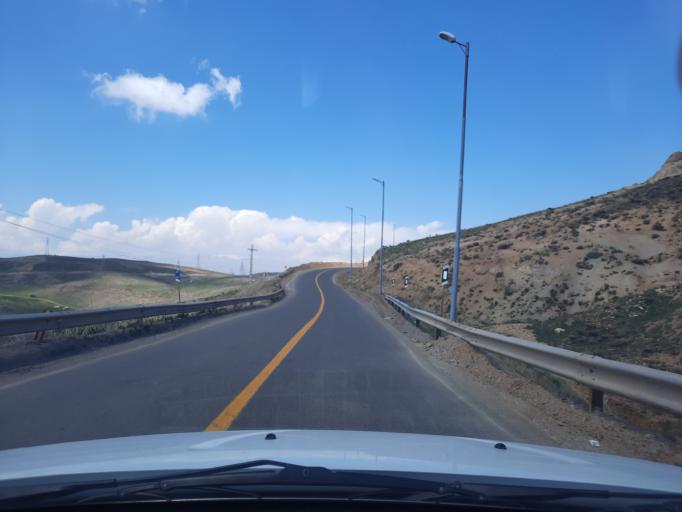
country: IR
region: Qazvin
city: Qazvin
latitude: 36.3864
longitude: 50.2070
